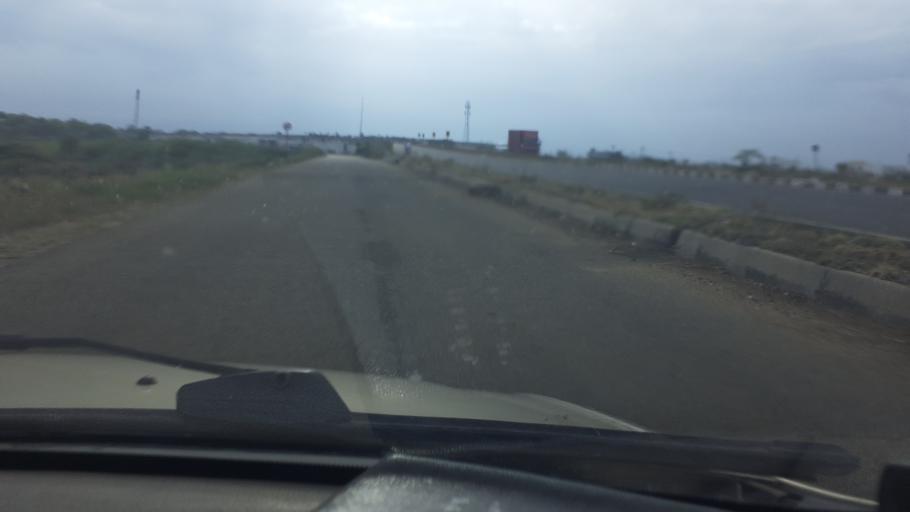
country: IN
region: Tamil Nadu
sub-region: Tirunelveli Kattabo
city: Tirunelveli
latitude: 8.6607
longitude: 77.7181
